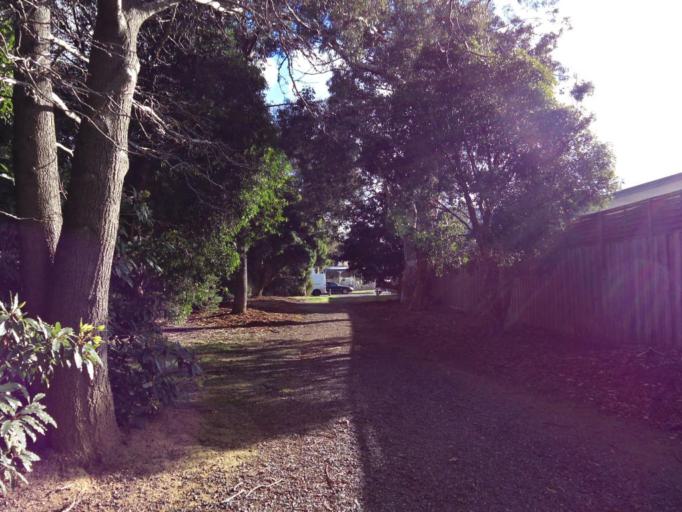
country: AU
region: Victoria
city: Mitcham
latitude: -37.8183
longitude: 145.2065
